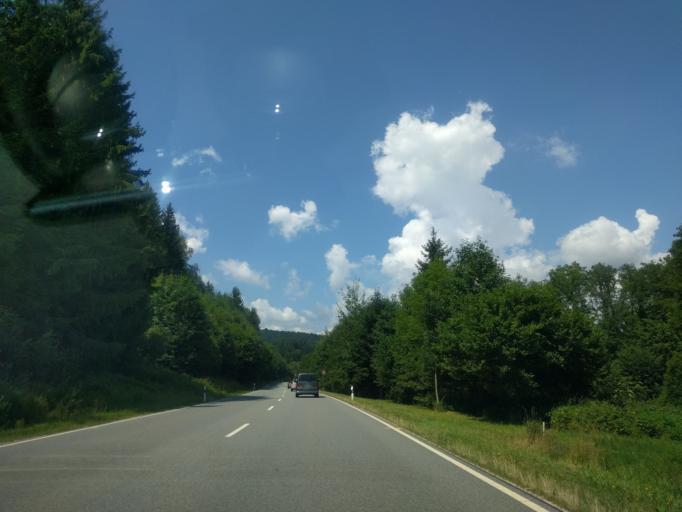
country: DE
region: Bavaria
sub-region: Lower Bavaria
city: Innernzell
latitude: 48.8435
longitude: 13.3123
